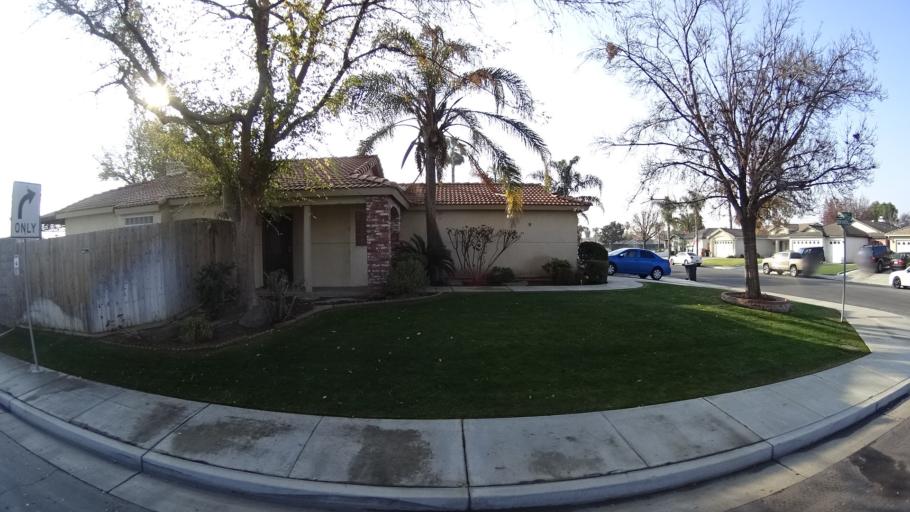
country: US
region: California
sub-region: Kern County
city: Greenacres
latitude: 35.3233
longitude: -119.0927
